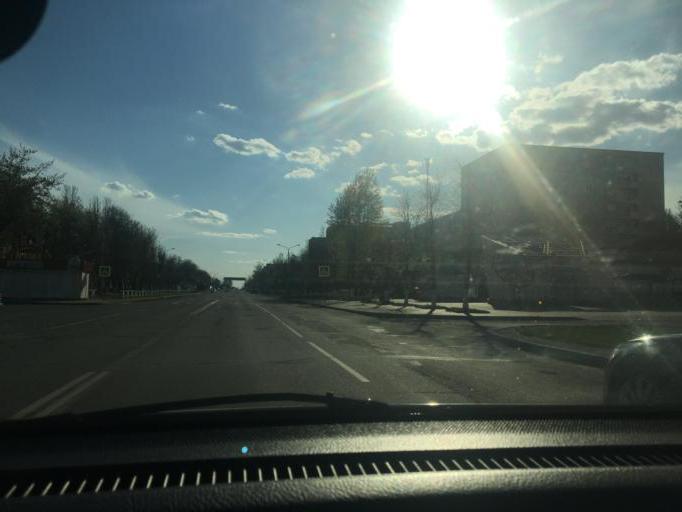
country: BY
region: Mogilev
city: Babruysk
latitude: 53.1707
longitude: 29.2007
